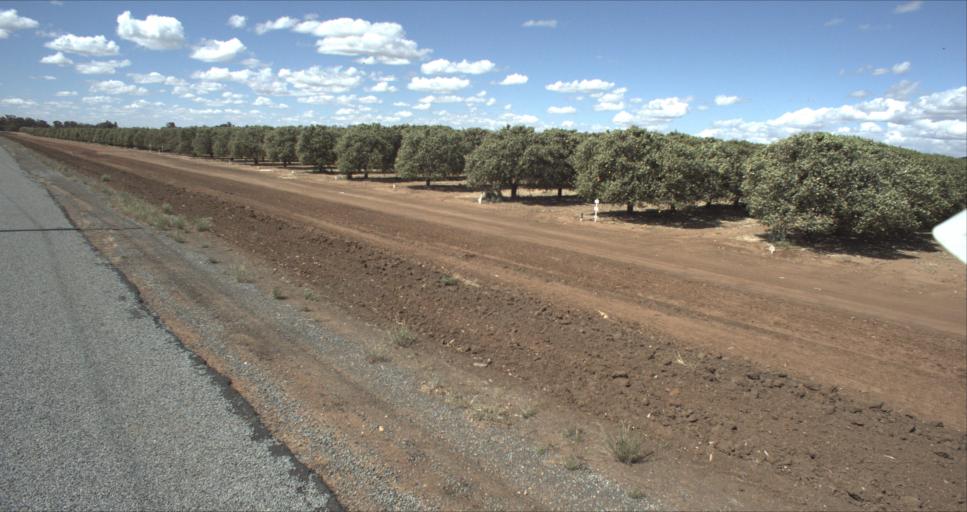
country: AU
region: New South Wales
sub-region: Leeton
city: Leeton
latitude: -34.5225
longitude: 146.2231
